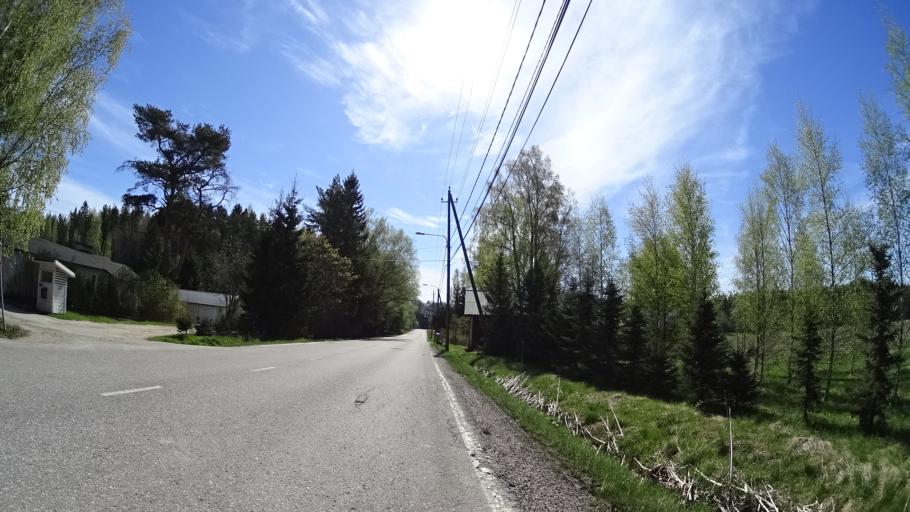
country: FI
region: Uusimaa
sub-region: Helsinki
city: Nurmijaervi
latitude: 60.3680
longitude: 24.8428
